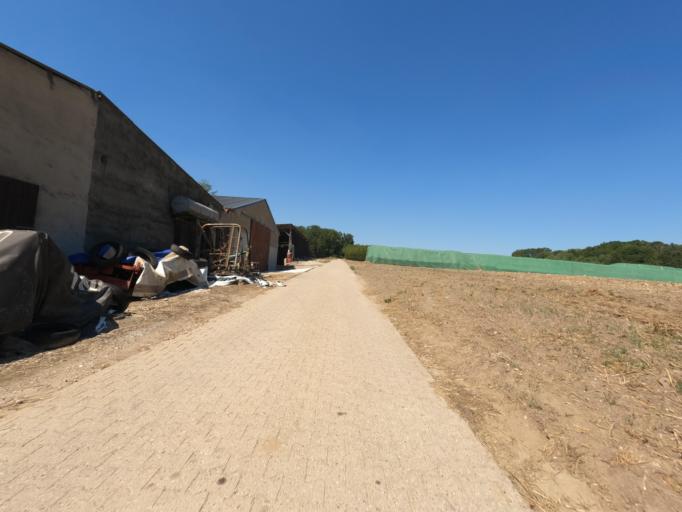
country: DE
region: North Rhine-Westphalia
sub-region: Regierungsbezirk Koln
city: Wassenberg
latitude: 51.0846
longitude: 6.1941
